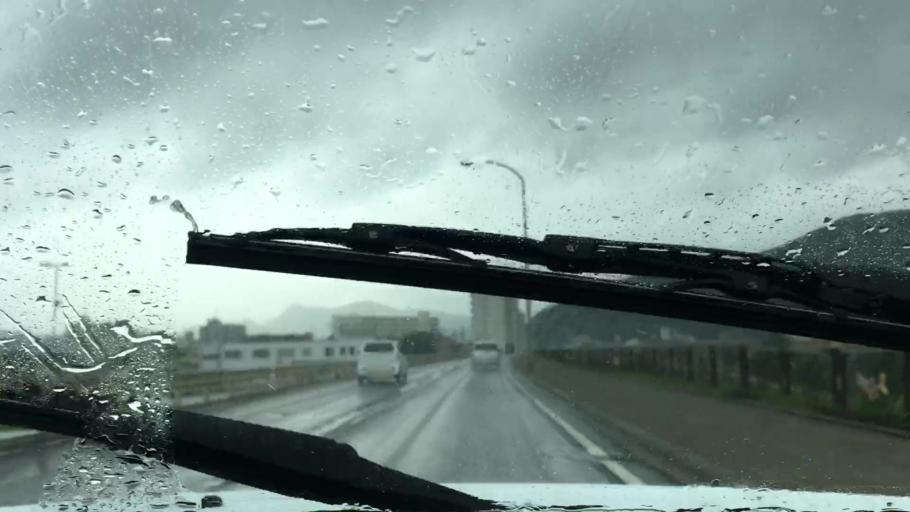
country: JP
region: Hokkaido
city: Sapporo
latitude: 43.0106
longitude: 141.3522
